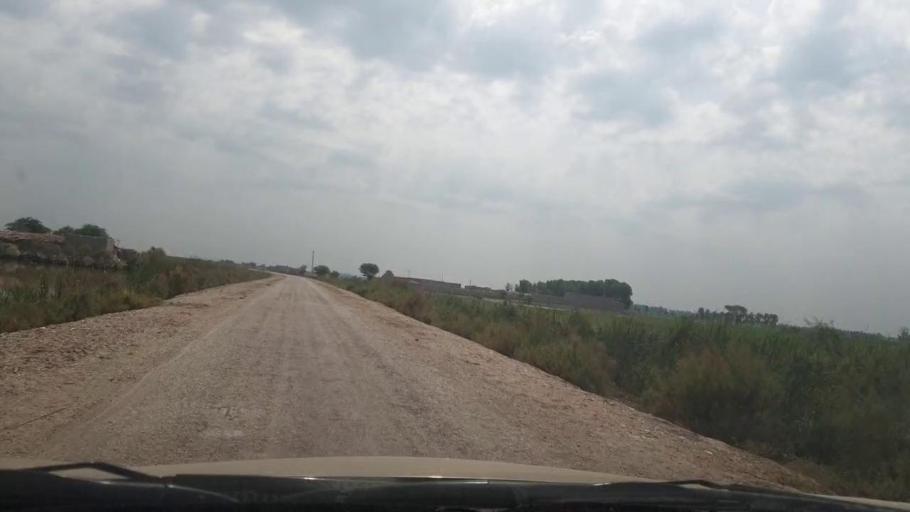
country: PK
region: Sindh
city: Ratodero
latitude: 27.6976
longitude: 68.2169
